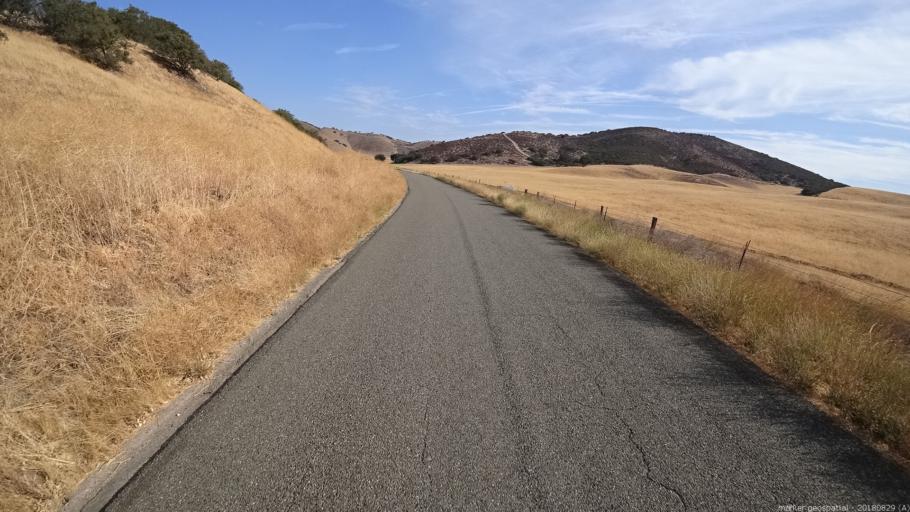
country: US
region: California
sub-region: Monterey County
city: King City
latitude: 36.0509
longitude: -121.0522
